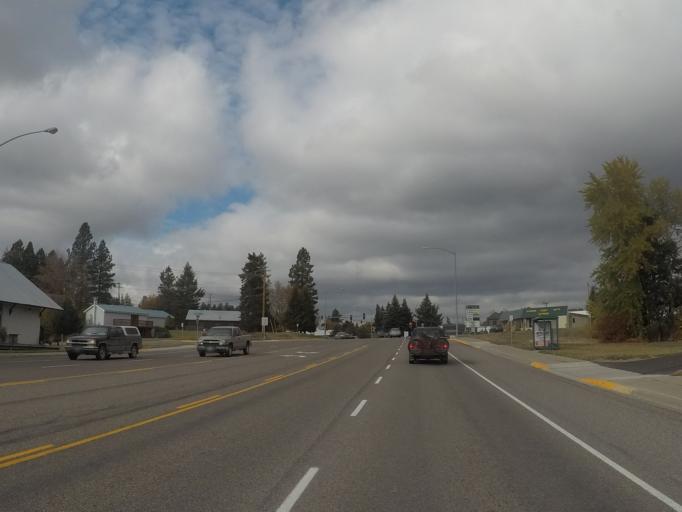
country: US
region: Montana
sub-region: Flathead County
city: Columbia Falls
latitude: 48.3685
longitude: -114.1792
